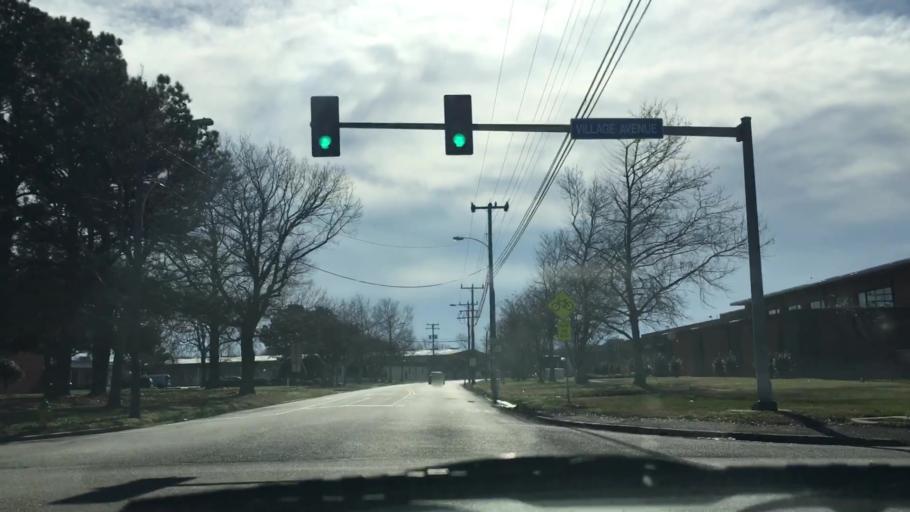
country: US
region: Virginia
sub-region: City of Norfolk
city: Norfolk
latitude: 36.8617
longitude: -76.2340
